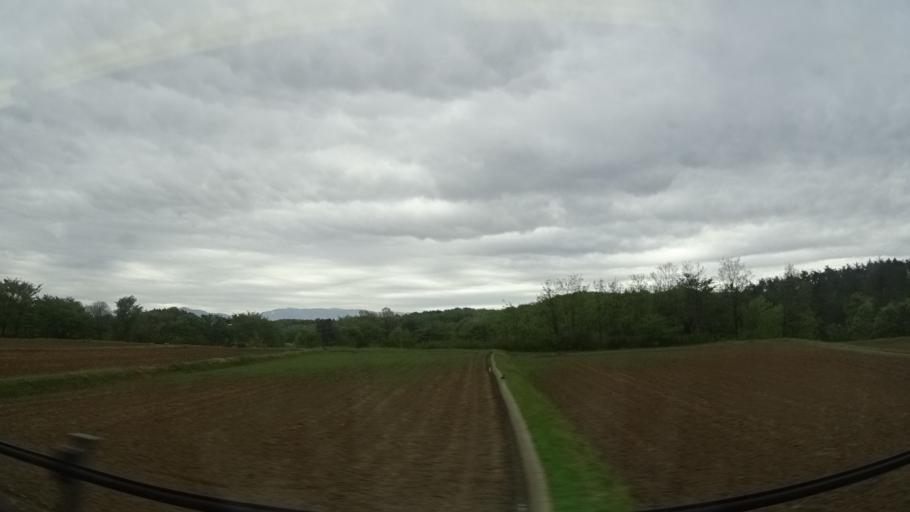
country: JP
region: Fukushima
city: Sukagawa
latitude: 37.2963
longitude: 140.3368
